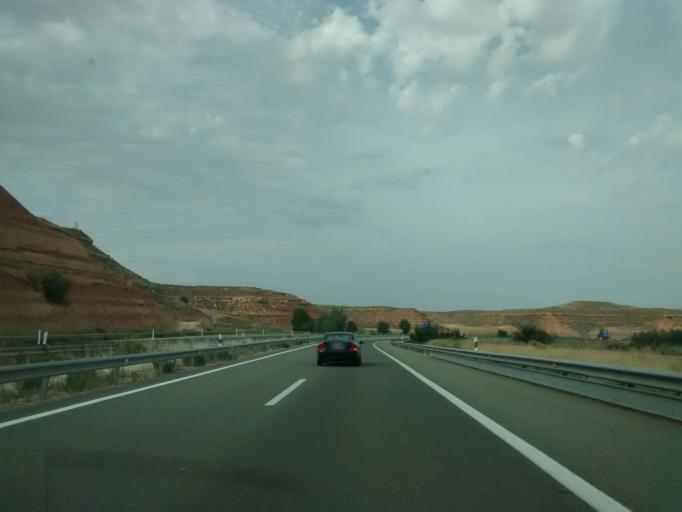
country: ES
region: Aragon
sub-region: Provincia de Zaragoza
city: Monreal de Ariza
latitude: 41.3021
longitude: -2.1432
